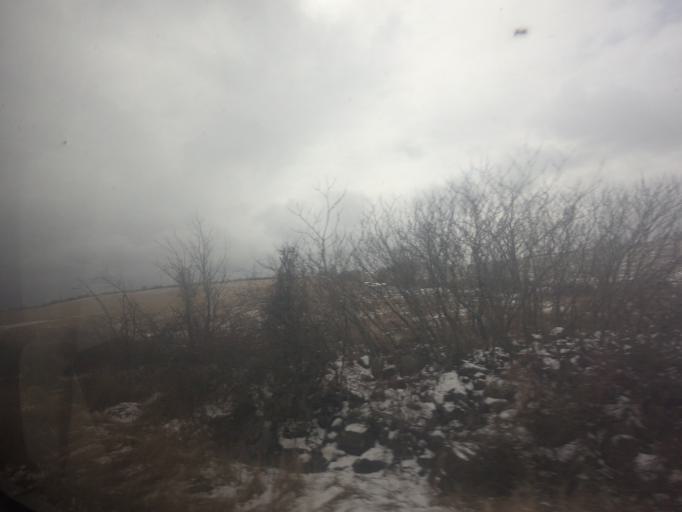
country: CA
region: Ontario
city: Cobourg
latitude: 43.9468
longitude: -78.3552
